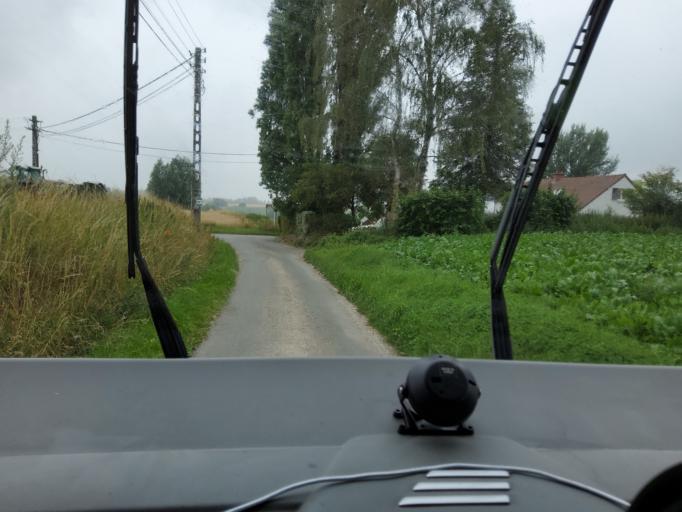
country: BE
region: Wallonia
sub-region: Province du Hainaut
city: Soignies
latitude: 50.6014
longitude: 4.0542
